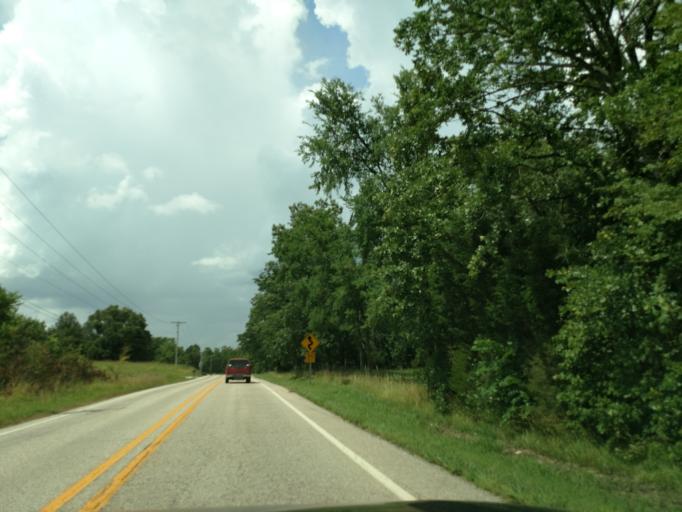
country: US
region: Arkansas
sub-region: Boone County
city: Harrison
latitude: 36.2848
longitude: -93.2354
